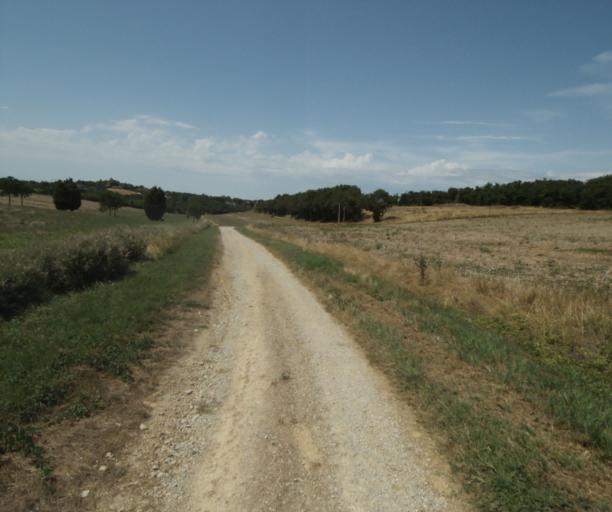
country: FR
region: Midi-Pyrenees
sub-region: Departement de la Haute-Garonne
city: Saint-Felix-Lauragais
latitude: 43.4530
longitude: 1.8514
